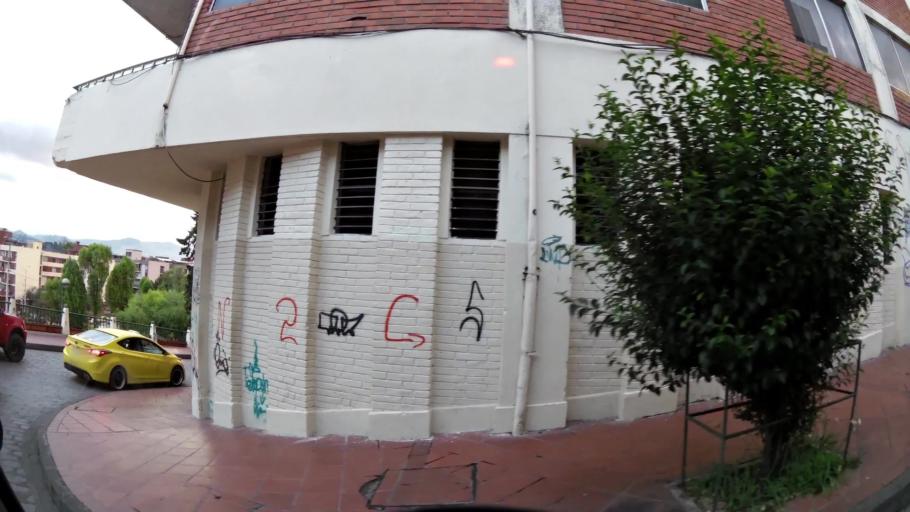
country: EC
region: Azuay
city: Cuenca
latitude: -2.9013
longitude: -79.0057
